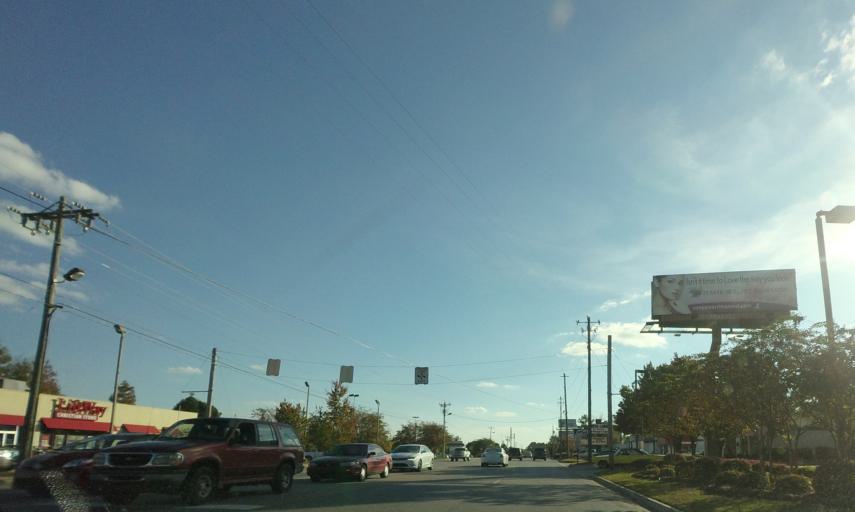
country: US
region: Georgia
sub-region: Lowndes County
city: Remerton
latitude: 30.8469
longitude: -83.3243
